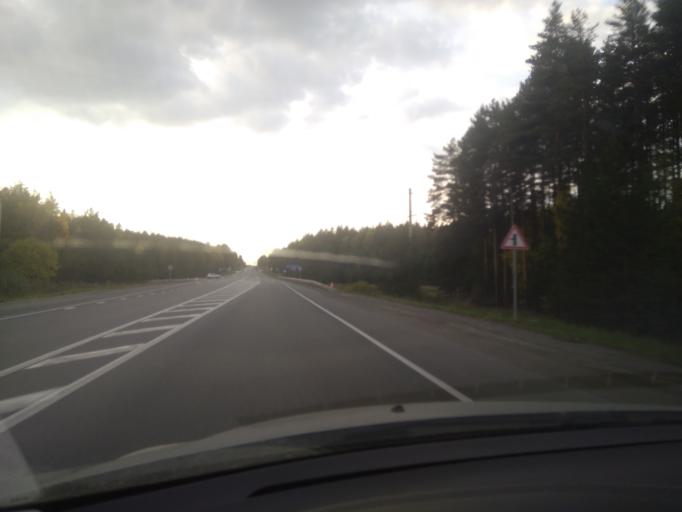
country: RU
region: Sverdlovsk
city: Verkhneye Dubrovo
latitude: 56.6972
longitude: 61.0918
